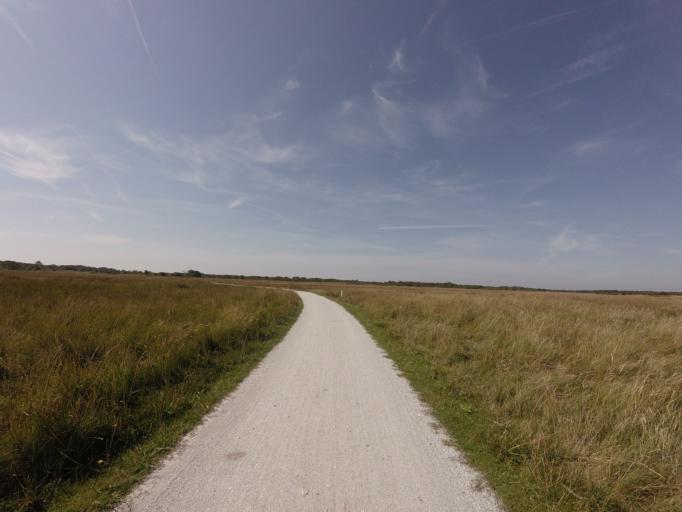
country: NL
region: Friesland
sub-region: Gemeente Schiermonnikoog
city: Schiermonnikoog
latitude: 53.4867
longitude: 6.2068
